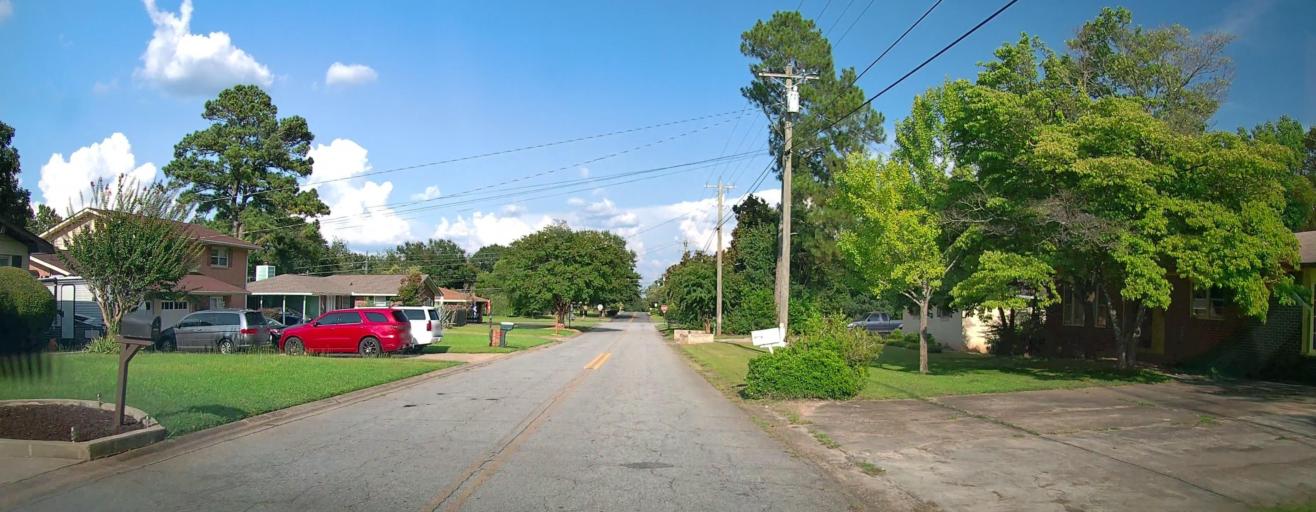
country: US
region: Georgia
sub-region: Houston County
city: Warner Robins
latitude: 32.5984
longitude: -83.6380
